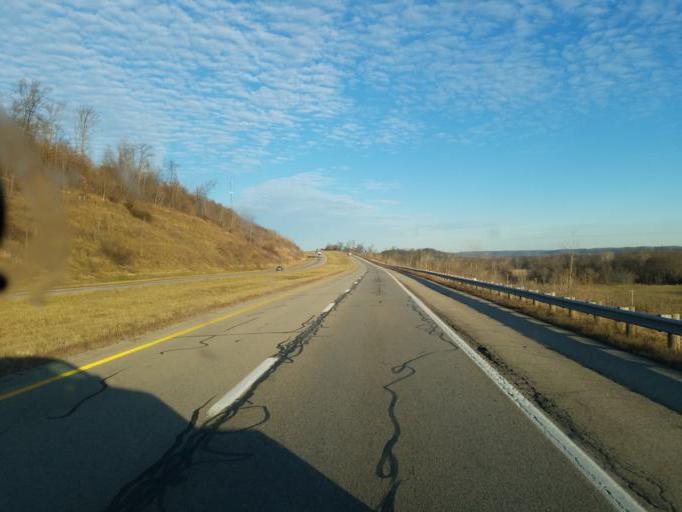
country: US
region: Ohio
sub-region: Muskingum County
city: Dresden
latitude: 40.1514
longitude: -82.0558
